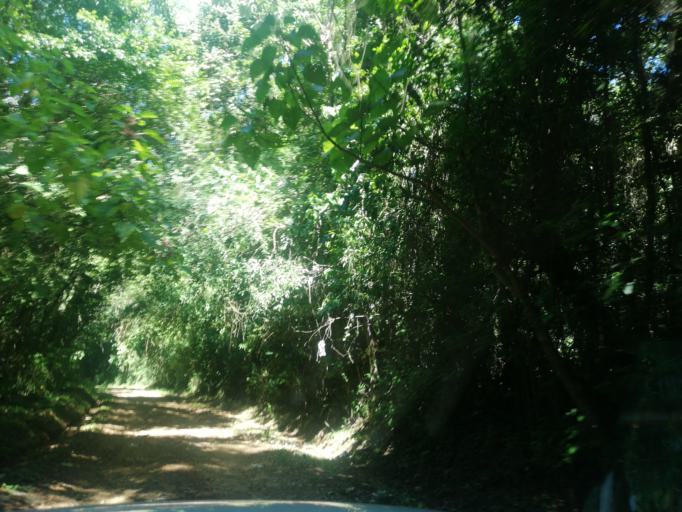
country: AR
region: Misiones
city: Cerro Azul
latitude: -27.7421
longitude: -55.5688
